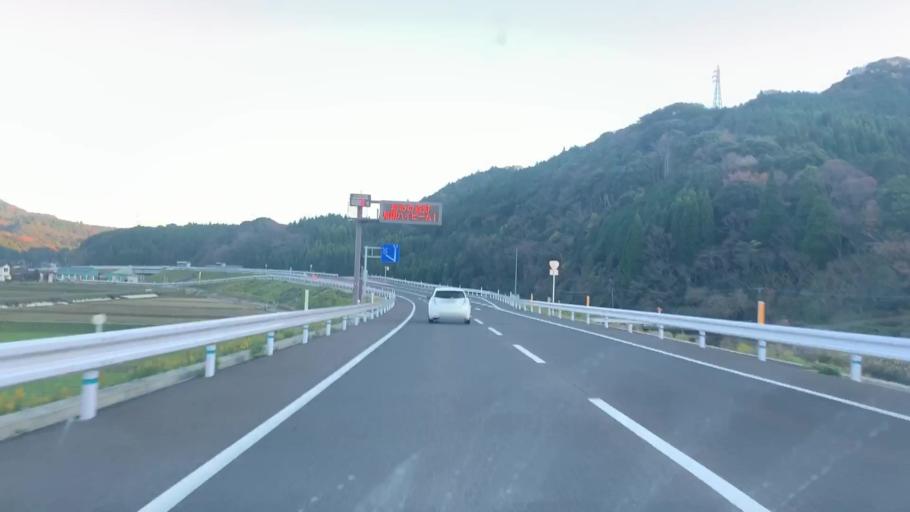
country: JP
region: Saga Prefecture
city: Takeocho-takeo
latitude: 33.2517
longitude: 129.9909
